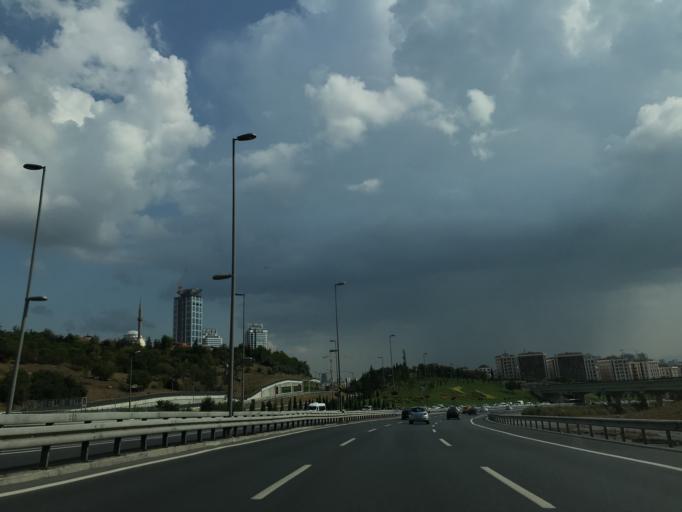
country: TR
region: Istanbul
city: UEskuedar
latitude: 41.0117
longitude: 29.0606
